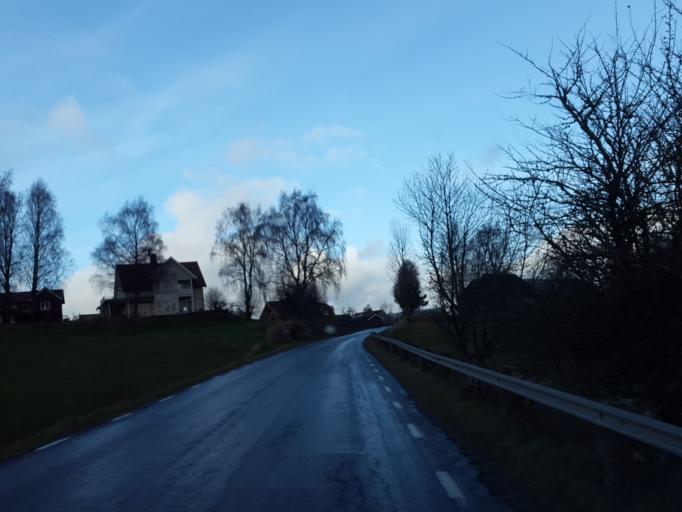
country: SE
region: Vaestra Goetaland
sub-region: Vargarda Kommun
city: Jonstorp
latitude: 57.9636
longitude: 12.7278
